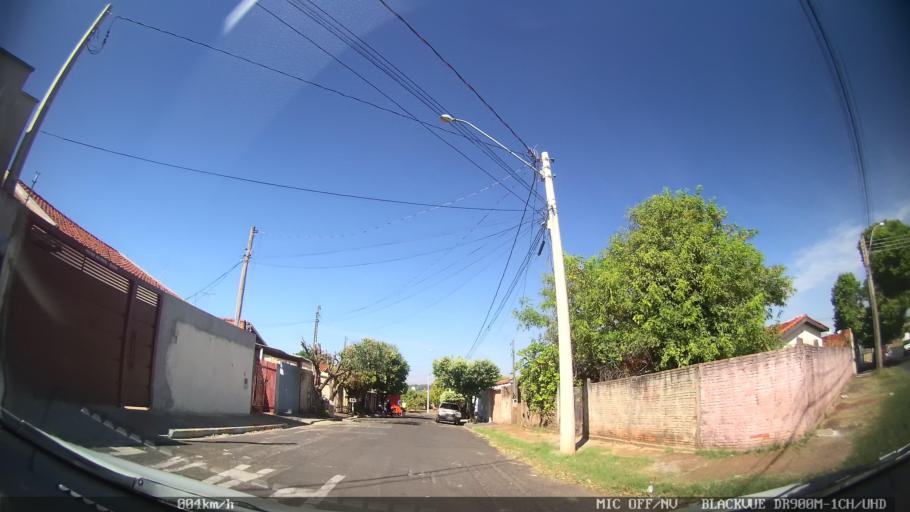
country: BR
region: Sao Paulo
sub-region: Sao Jose Do Rio Preto
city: Sao Jose do Rio Preto
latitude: -20.7718
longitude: -49.4138
